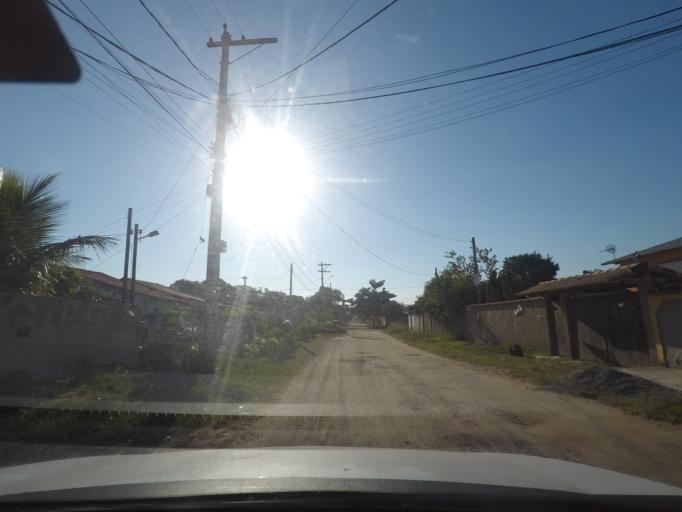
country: BR
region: Rio de Janeiro
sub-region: Marica
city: Marica
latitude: -22.9620
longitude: -42.9482
